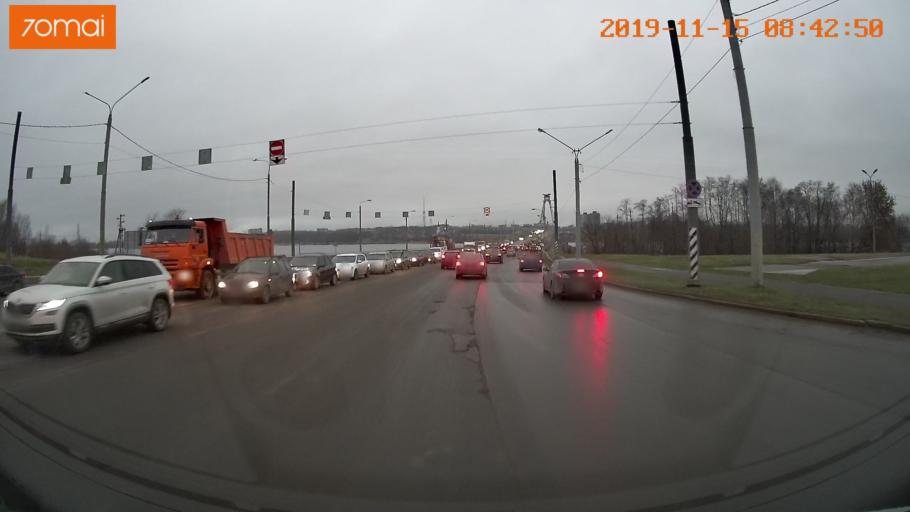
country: RU
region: Vologda
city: Cherepovets
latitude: 59.1060
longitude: 37.9060
